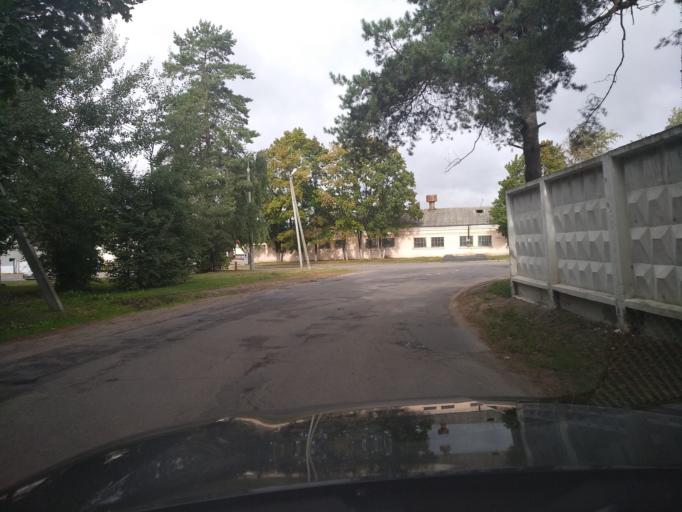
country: BY
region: Minsk
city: Minsk
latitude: 53.8803
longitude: 27.6386
